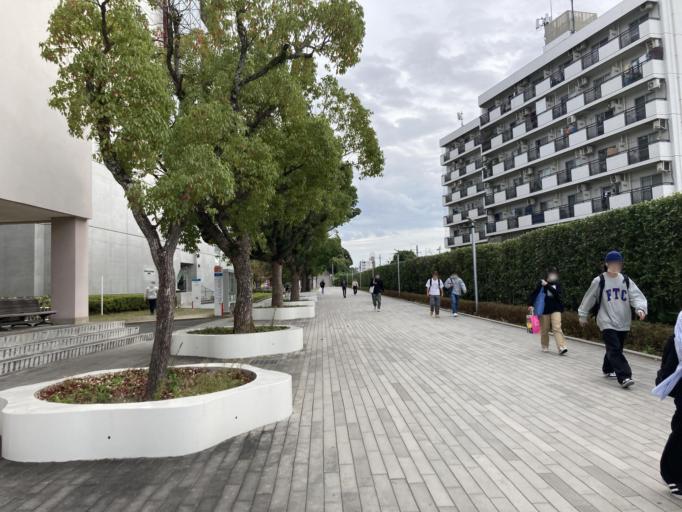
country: JP
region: Fukuoka
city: Shingu
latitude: 33.6727
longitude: 130.4425
